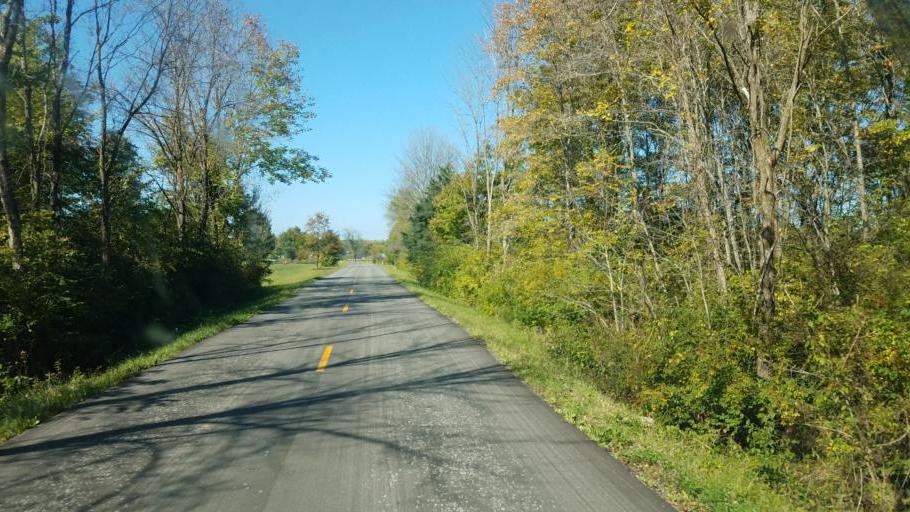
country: US
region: Kentucky
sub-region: Fleming County
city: Flemingsburg
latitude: 38.4687
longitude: -83.5890
